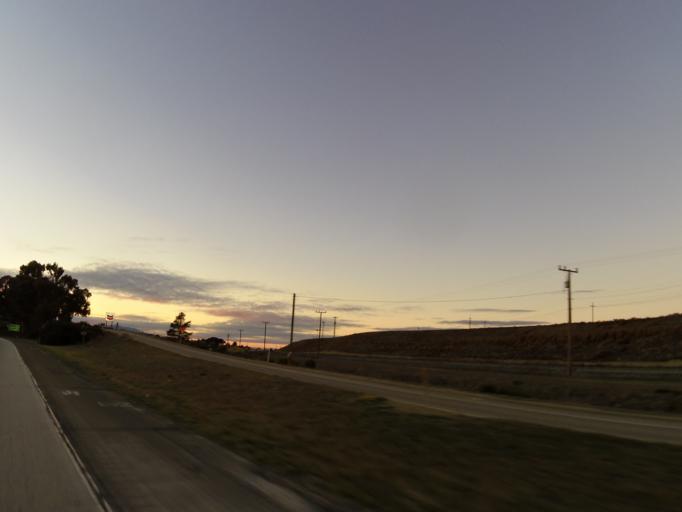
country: US
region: California
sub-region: Monterey County
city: King City
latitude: 36.2008
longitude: -121.1101
